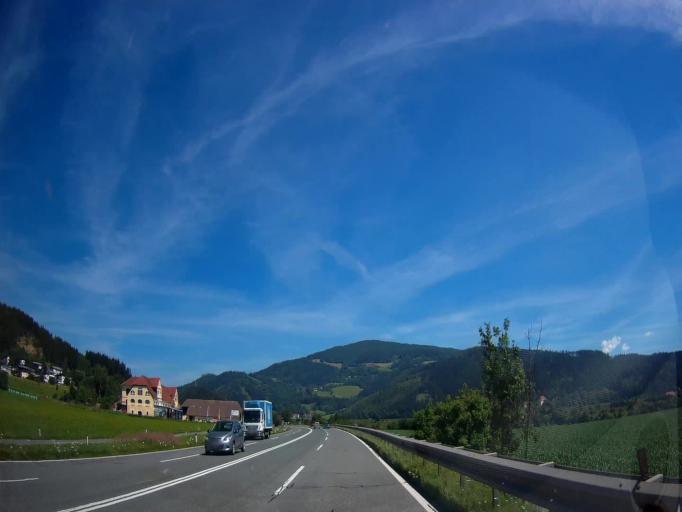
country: AT
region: Carinthia
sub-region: Politischer Bezirk Sankt Veit an der Glan
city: Althofen
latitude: 46.8732
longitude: 14.4503
